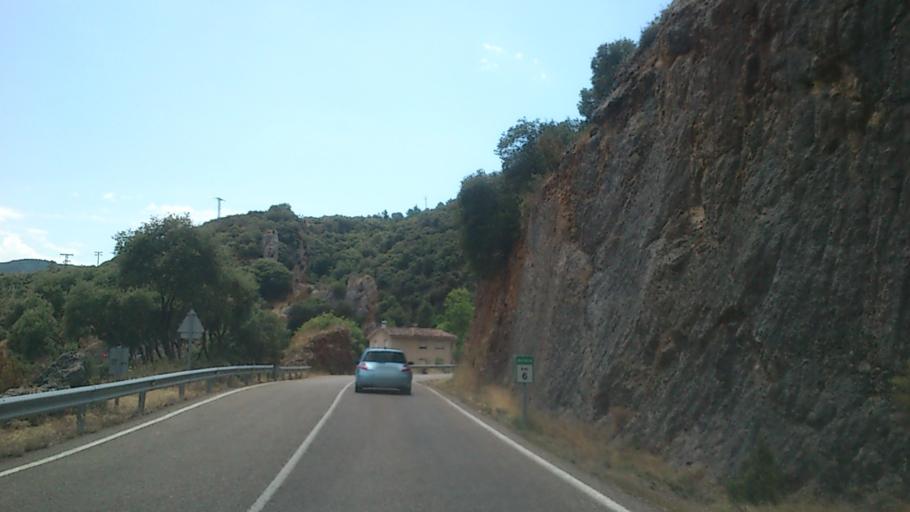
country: ES
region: Castille and Leon
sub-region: Provincia de Burgos
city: Frias
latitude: 42.7507
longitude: -3.3063
